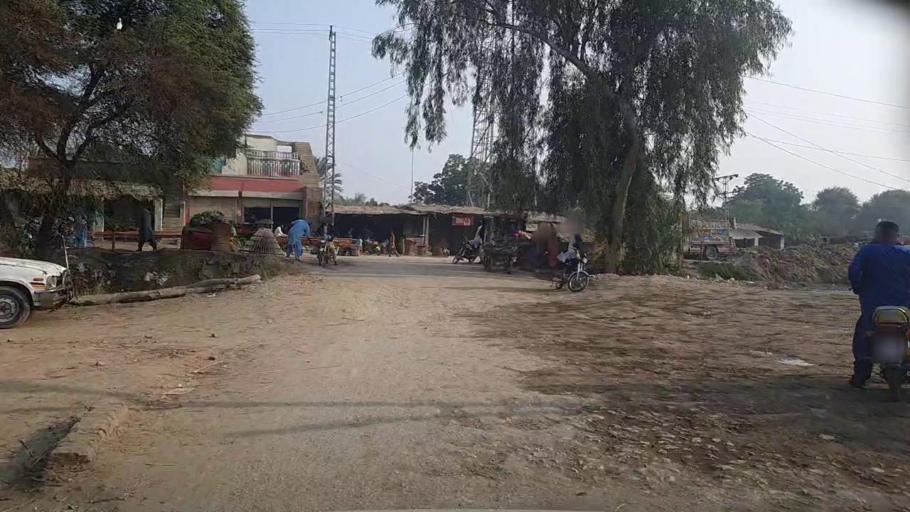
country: PK
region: Sindh
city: Kandiari
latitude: 27.0302
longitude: 68.4875
